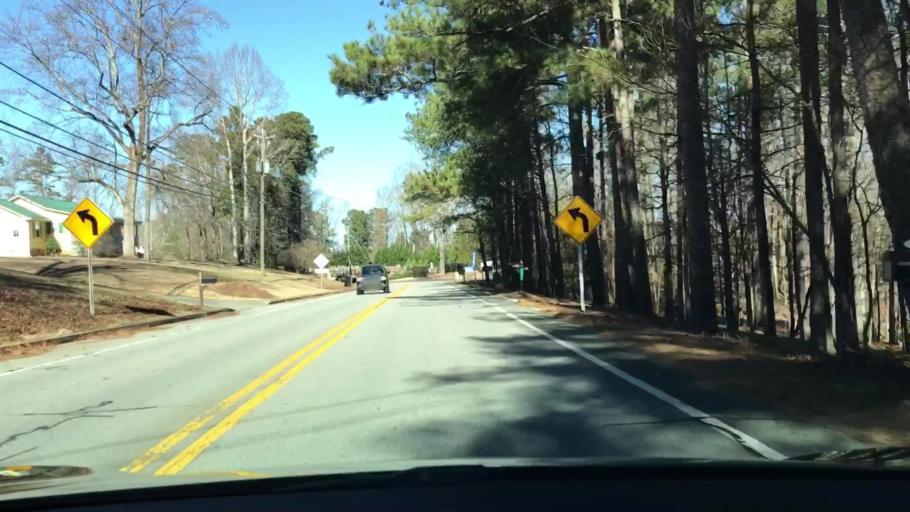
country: US
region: Georgia
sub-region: Gwinnett County
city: Buford
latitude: 34.1441
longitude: -84.0269
